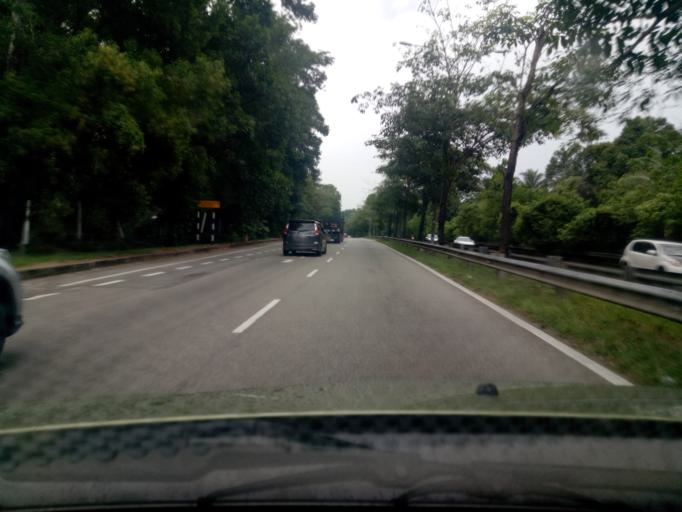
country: MY
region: Kedah
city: Sungai Petani
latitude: 5.6689
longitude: 100.5087
